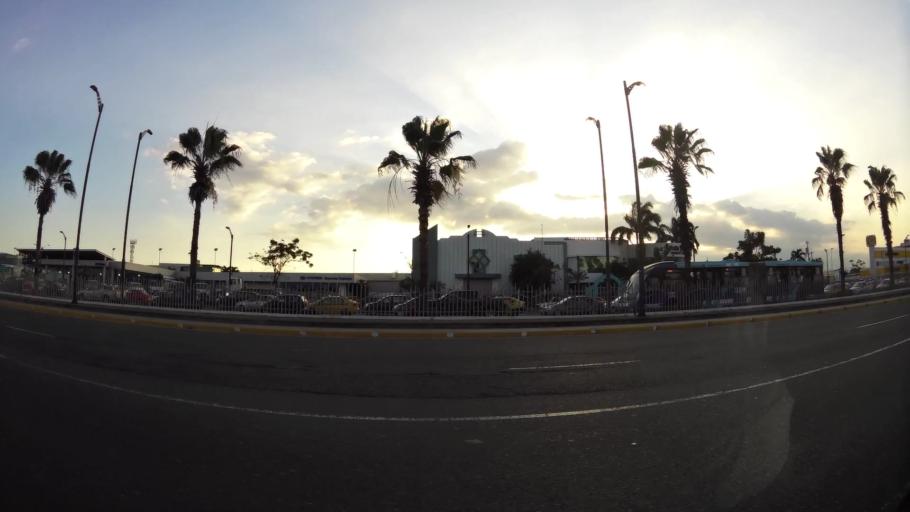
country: EC
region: Guayas
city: Eloy Alfaro
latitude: -2.1494
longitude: -79.8863
